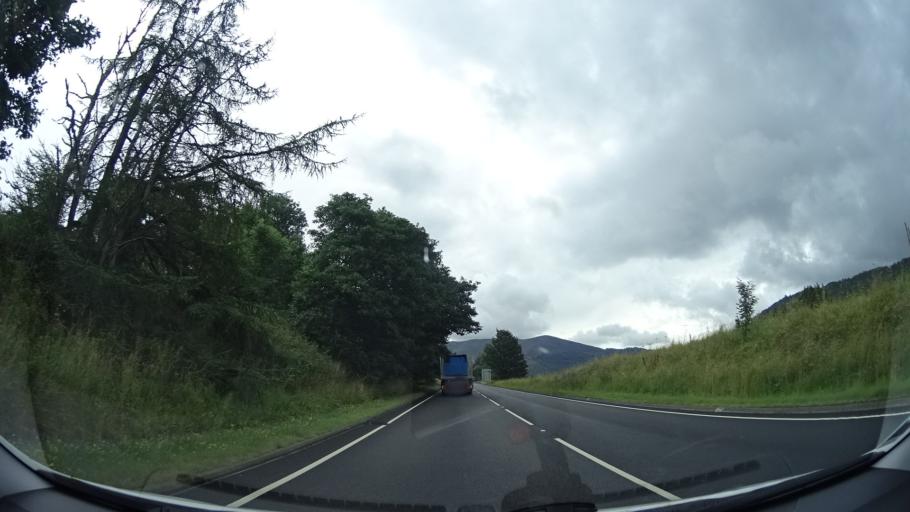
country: GB
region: Scotland
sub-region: Perth and Kinross
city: Pitlochry
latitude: 56.7549
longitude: -3.7988
